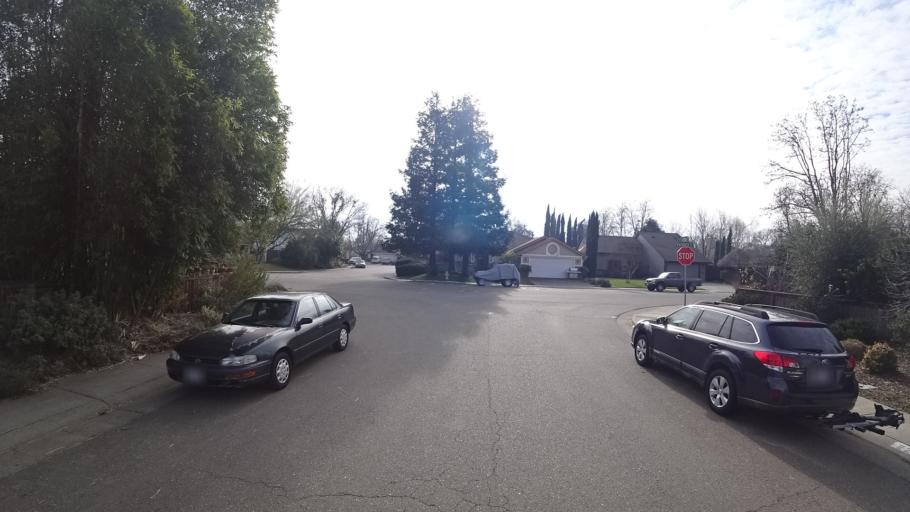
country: US
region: California
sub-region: Yolo County
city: Davis
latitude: 38.5371
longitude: -121.7235
